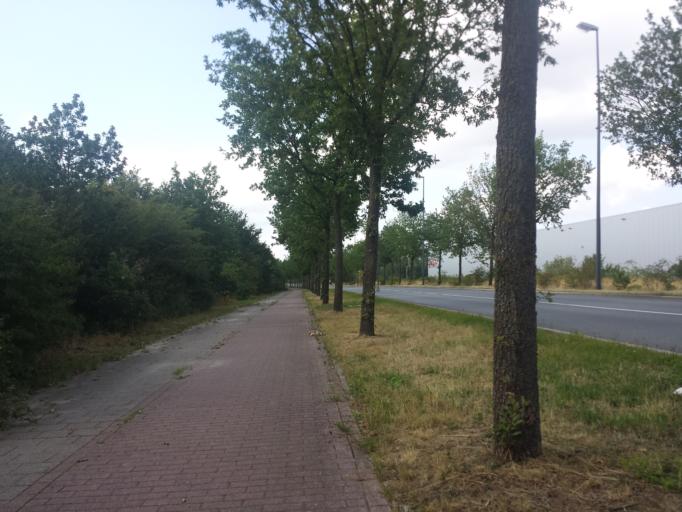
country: DE
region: Lower Saxony
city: Stuhr
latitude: 53.0829
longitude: 8.7334
